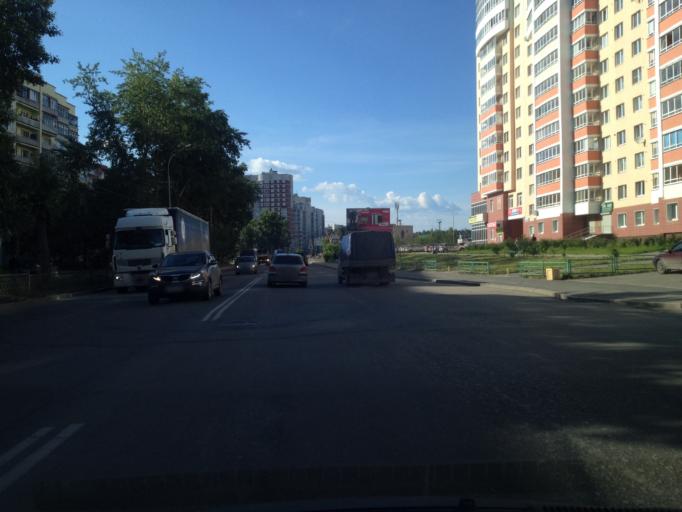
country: RU
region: Sverdlovsk
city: Yekaterinburg
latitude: 56.9061
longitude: 60.6214
